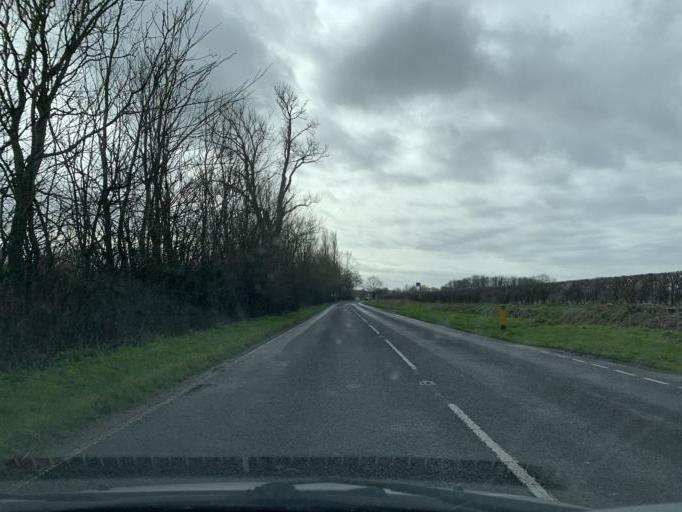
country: GB
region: England
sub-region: Hampshire
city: Fordingbridge
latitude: 50.9665
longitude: -1.7696
